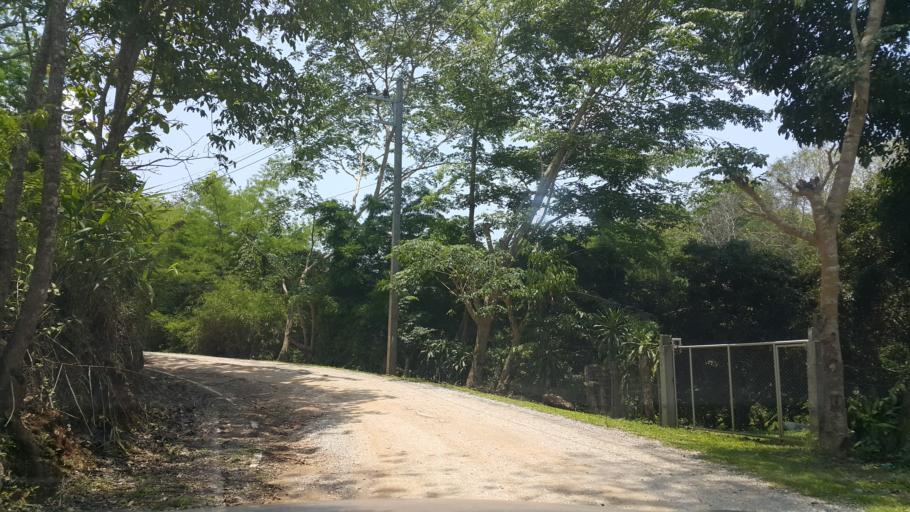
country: TH
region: Chiang Rai
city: Chiang Rai
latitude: 19.9943
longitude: 99.7240
